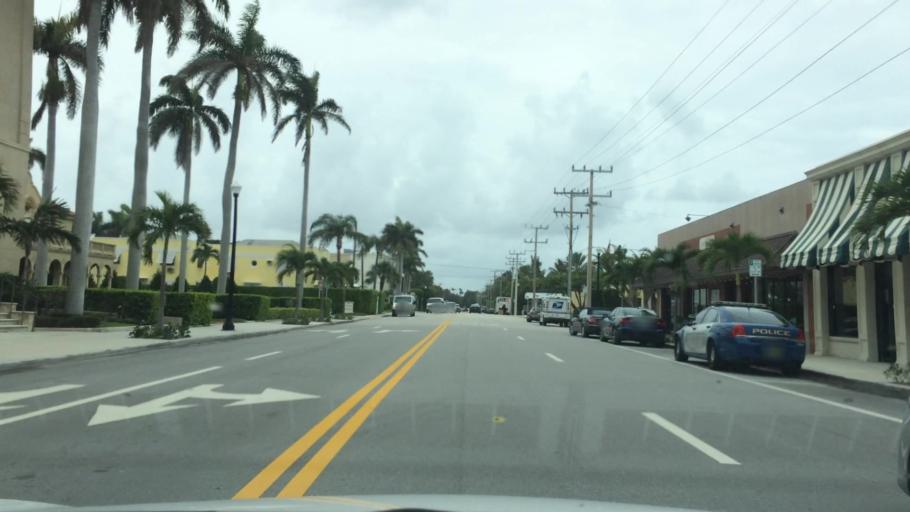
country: US
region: Florida
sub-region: Palm Beach County
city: Palm Beach
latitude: 26.7203
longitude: -80.0379
